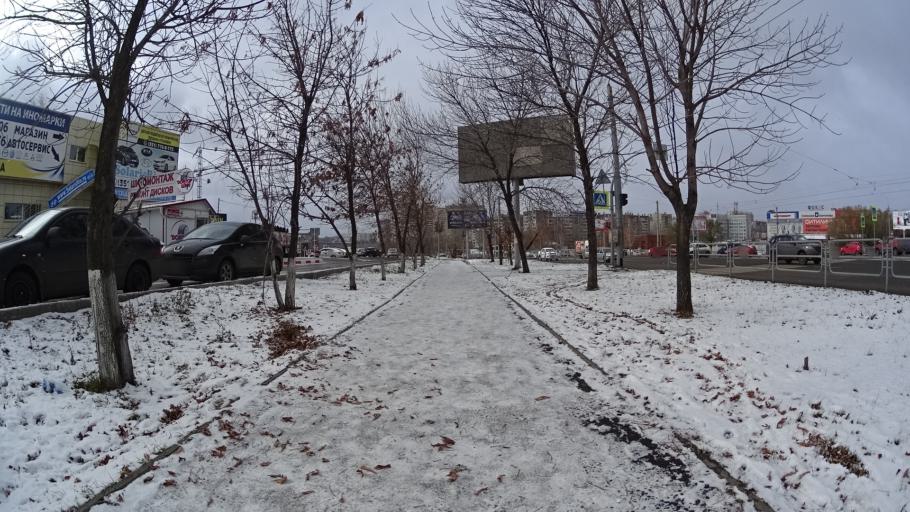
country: RU
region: Chelyabinsk
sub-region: Gorod Chelyabinsk
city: Chelyabinsk
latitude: 55.1885
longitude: 61.3079
